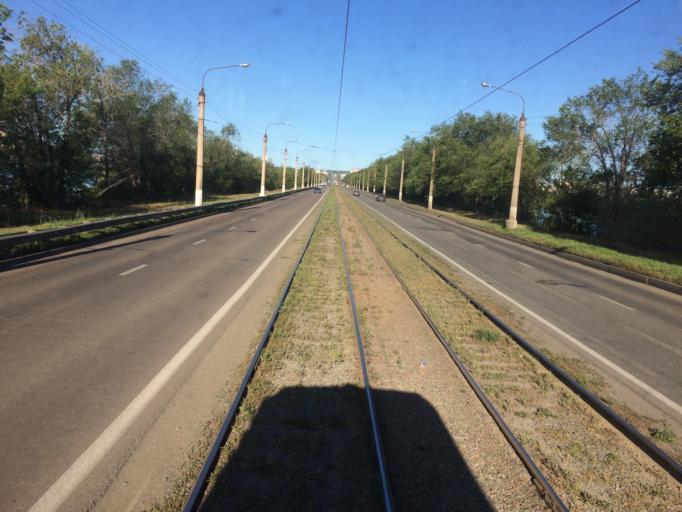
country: RU
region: Chelyabinsk
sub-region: Gorod Magnitogorsk
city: Magnitogorsk
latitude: 53.3981
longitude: 59.0134
